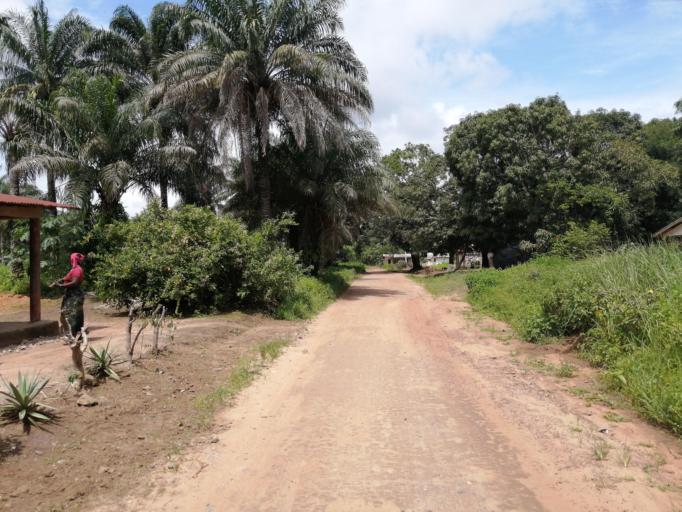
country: SL
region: Northern Province
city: Pepel
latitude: 8.6131
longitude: -13.0484
